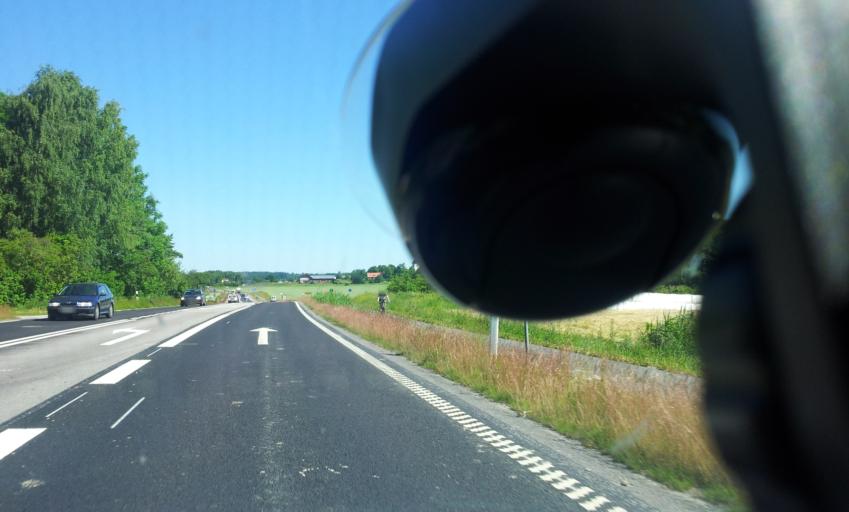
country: SE
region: OEstergoetland
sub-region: Soderkopings Kommun
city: Soederkoeping
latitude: 58.5206
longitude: 16.2867
